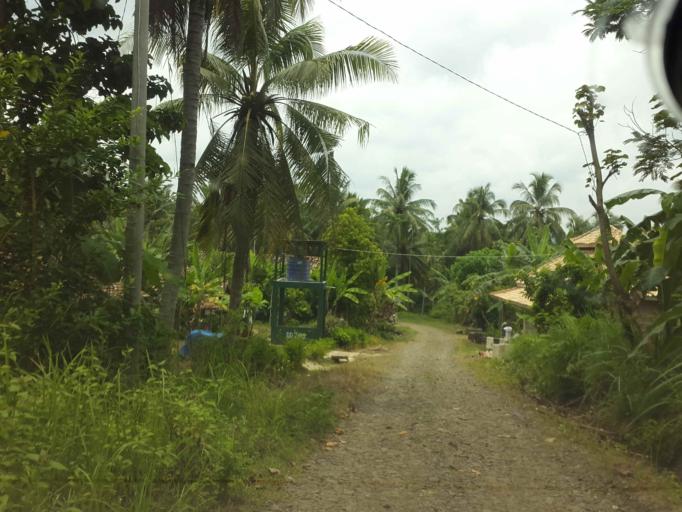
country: ID
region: Lampung
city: Sidorejo
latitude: -5.6263
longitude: 105.4607
